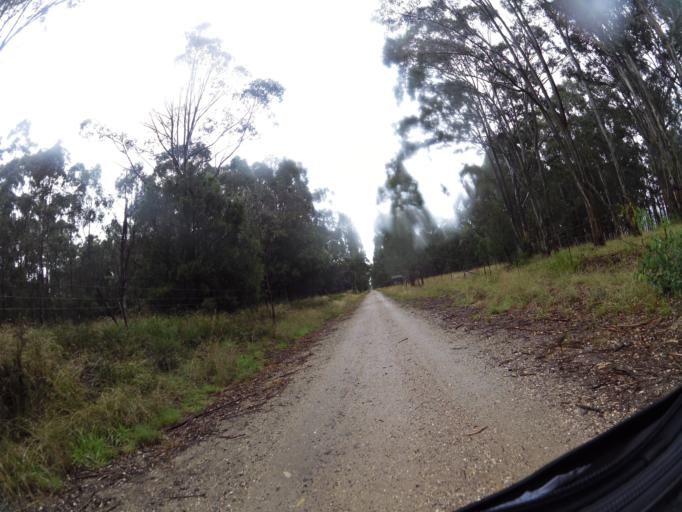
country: AU
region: Victoria
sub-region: East Gippsland
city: Lakes Entrance
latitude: -37.7936
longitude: 147.8291
